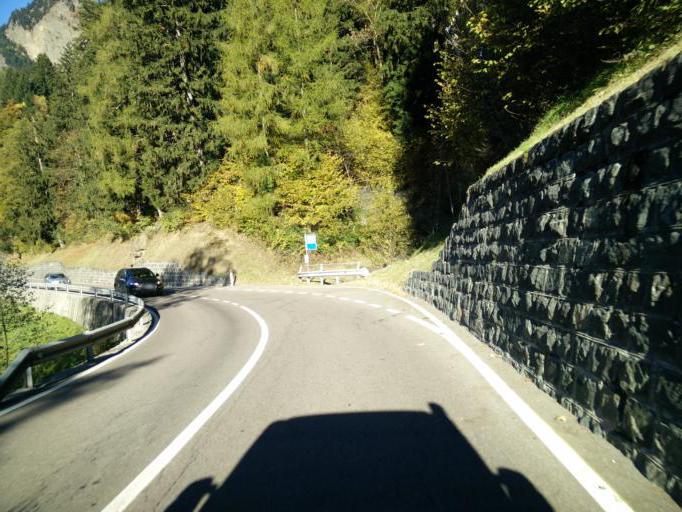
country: IT
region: Trentino-Alto Adige
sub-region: Bolzano
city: Moso in Passiria
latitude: 46.8276
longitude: 11.1767
